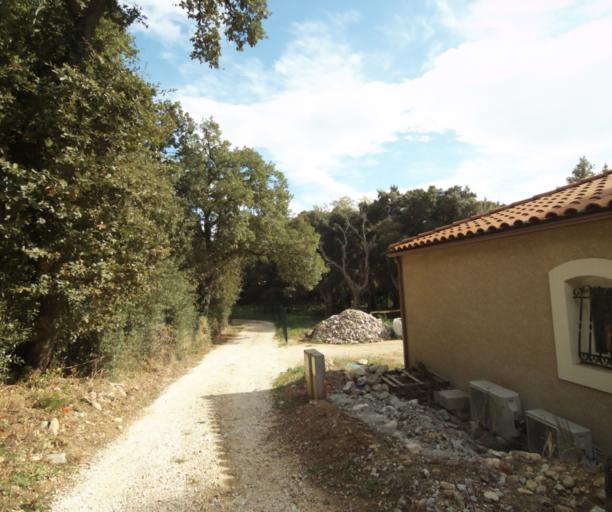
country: FR
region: Languedoc-Roussillon
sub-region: Departement des Pyrenees-Orientales
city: Argelers
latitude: 42.5440
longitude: 3.0122
